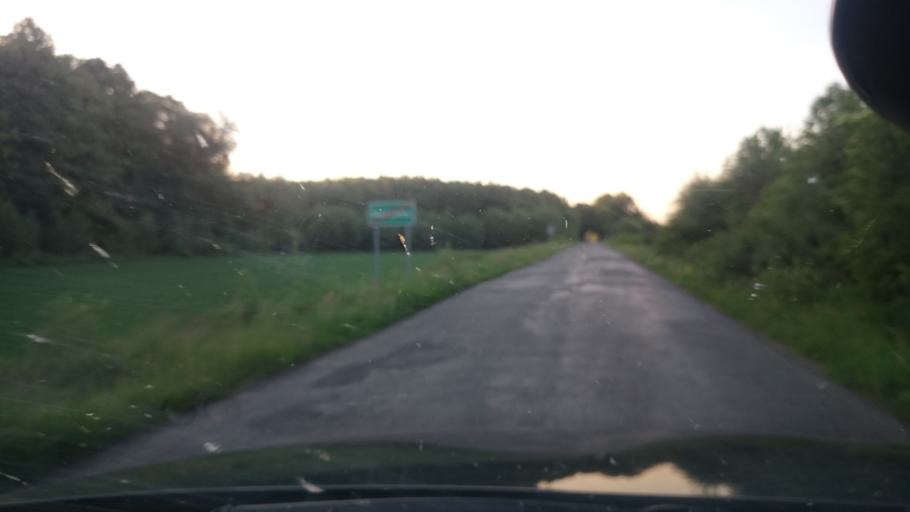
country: PL
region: Lower Silesian Voivodeship
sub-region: Powiat zabkowicki
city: Zloty Stok
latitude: 50.4769
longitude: 16.8468
